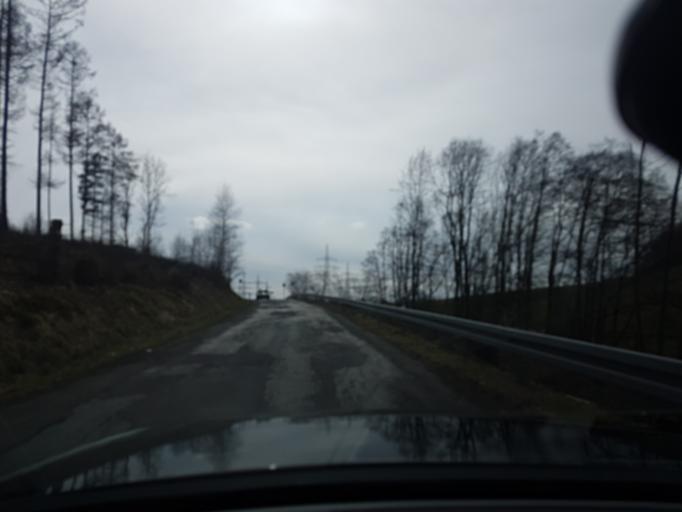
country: DE
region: North Rhine-Westphalia
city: Altena
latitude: 51.2537
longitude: 7.6844
